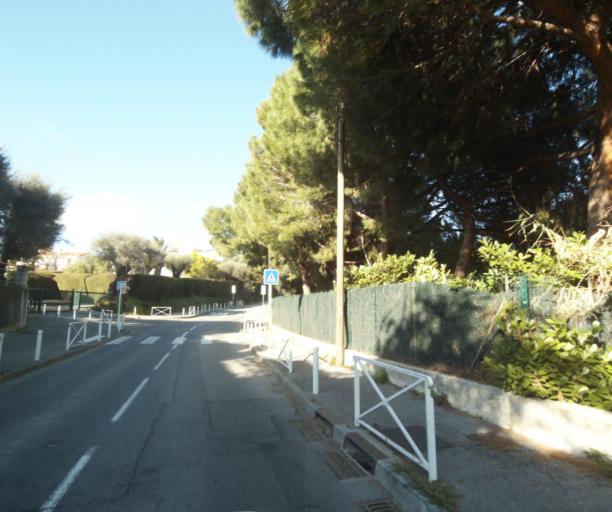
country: FR
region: Provence-Alpes-Cote d'Azur
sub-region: Departement des Alpes-Maritimes
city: Biot
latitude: 43.5988
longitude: 7.1070
